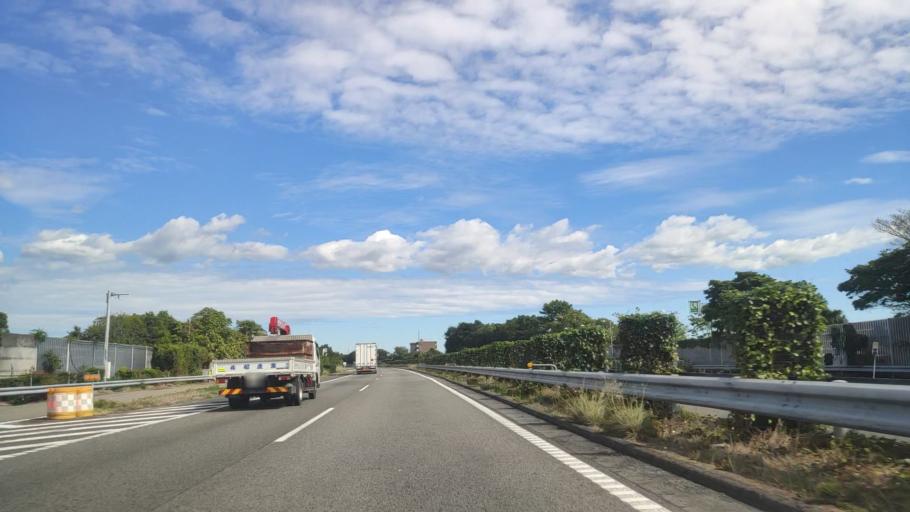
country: JP
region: Shizuoka
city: Hamamatsu
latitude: 34.7508
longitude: 137.7495
